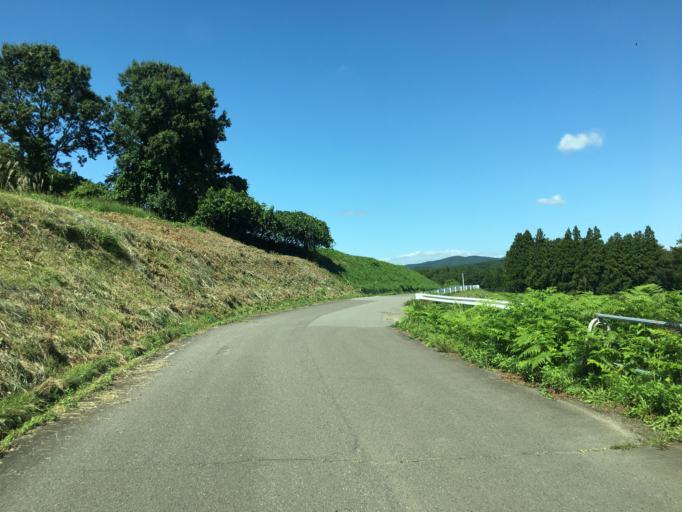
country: JP
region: Fukushima
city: Ishikawa
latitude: 37.2614
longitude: 140.5511
